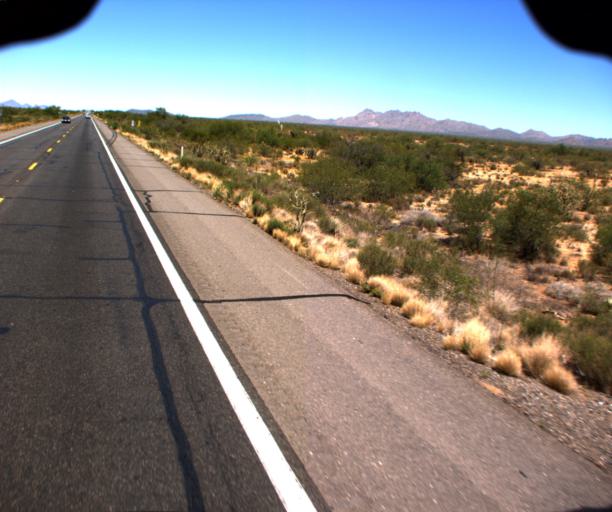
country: US
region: Arizona
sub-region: Yavapai County
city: Congress
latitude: 34.1112
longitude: -112.9329
